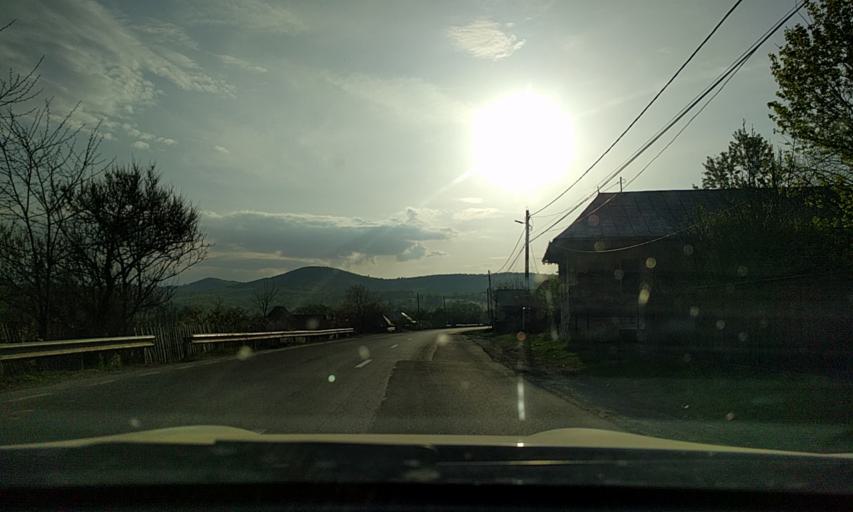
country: RO
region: Covasna
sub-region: Comuna Bretcu
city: Bretcu
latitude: 46.0476
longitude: 26.3135
